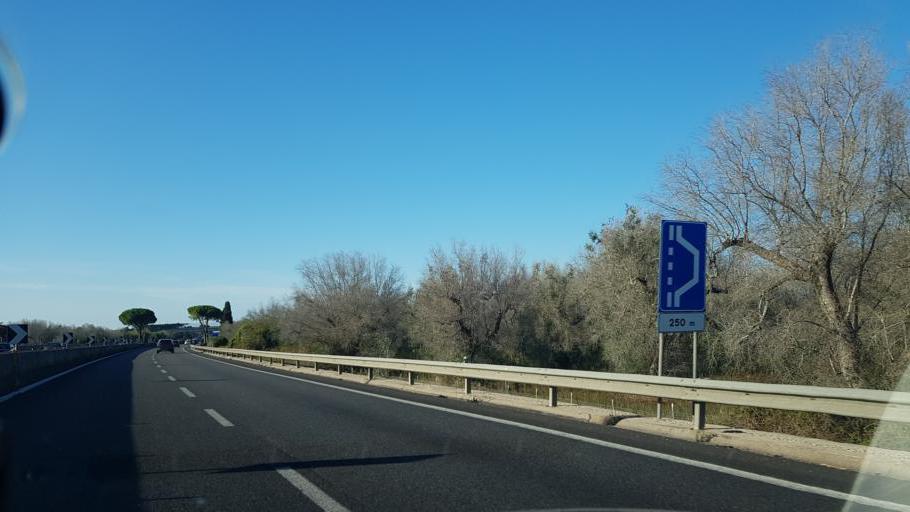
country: IT
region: Apulia
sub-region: Provincia di Lecce
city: Squinzano
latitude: 40.4525
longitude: 18.0662
